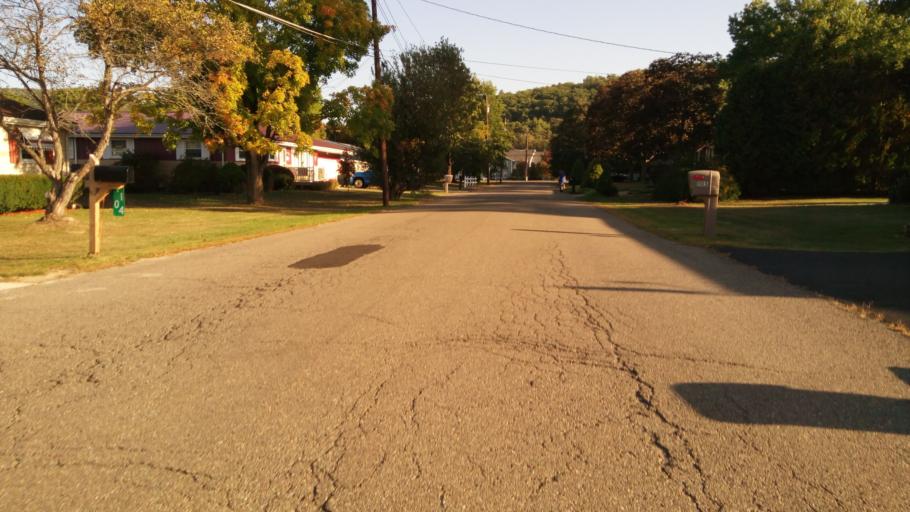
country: US
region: New York
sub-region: Chemung County
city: Southport
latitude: 42.0534
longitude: -76.8346
